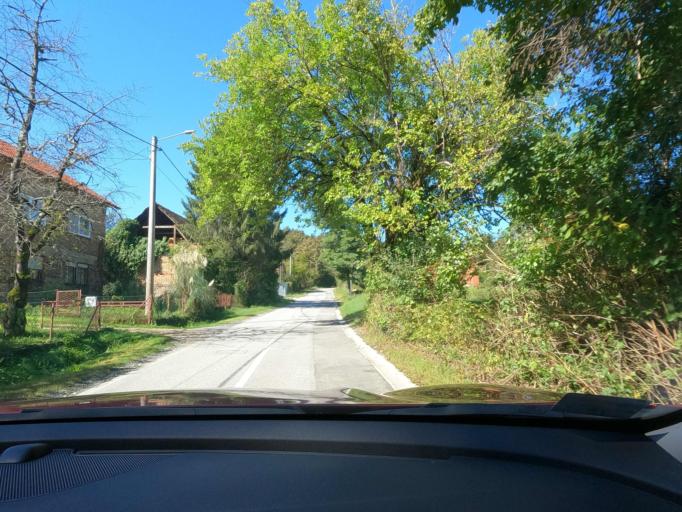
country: HR
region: Sisacko-Moslavacka
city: Petrinja
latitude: 45.4665
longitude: 16.2861
